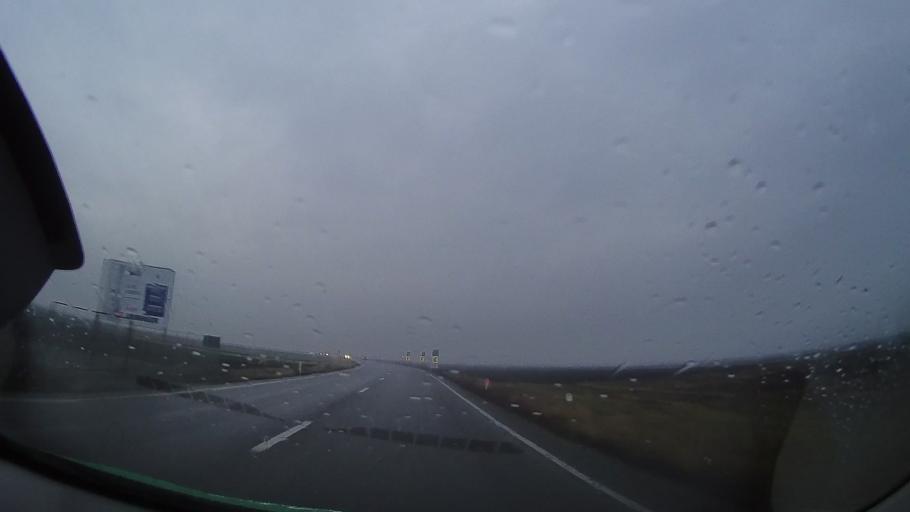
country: RO
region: Harghita
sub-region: Municipiul Gheorgheni
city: Gheorgheni
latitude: 46.7293
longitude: 25.5779
